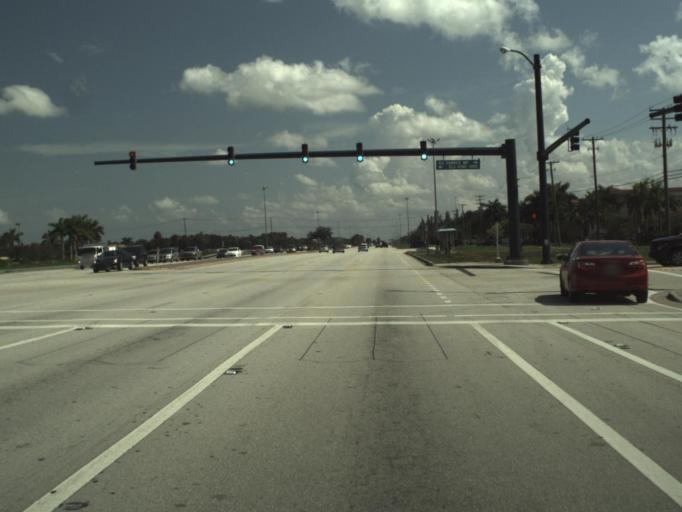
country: US
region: Florida
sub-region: Palm Beach County
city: Wellington
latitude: 26.6655
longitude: -80.2031
